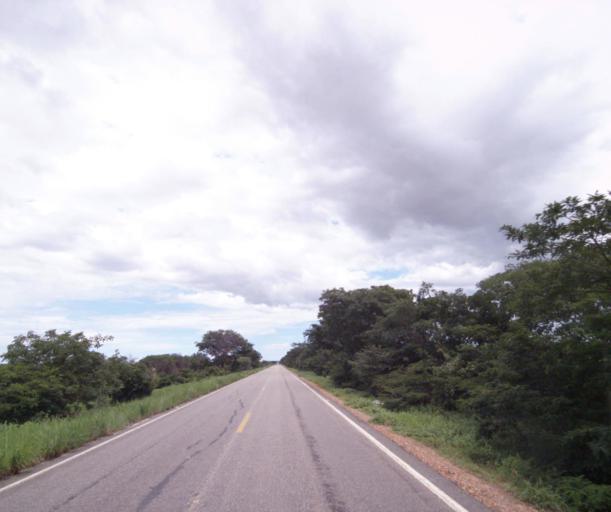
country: BR
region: Bahia
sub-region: Palmas De Monte Alto
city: Palmas de Monte Alto
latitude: -14.2641
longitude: -43.3411
